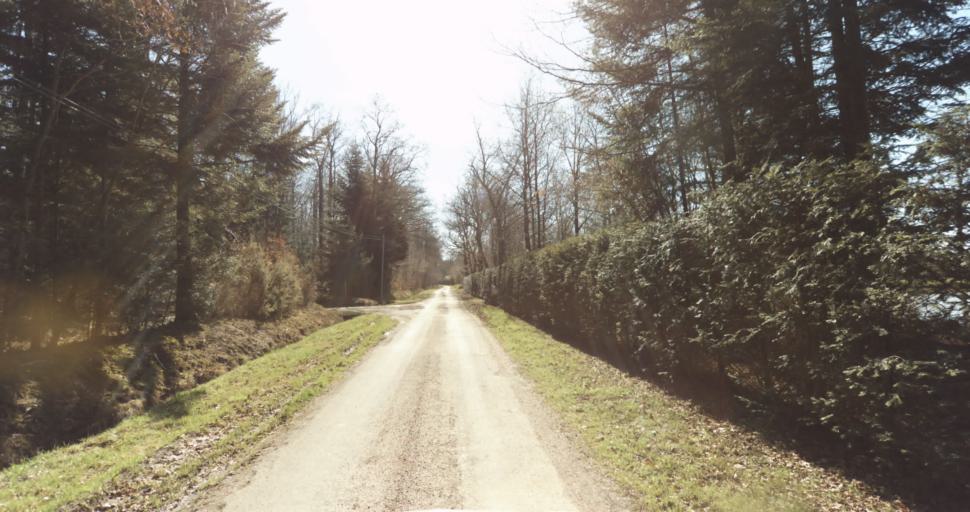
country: FR
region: Lower Normandy
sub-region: Departement du Calvados
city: Livarot
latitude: 48.9599
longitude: 0.0830
